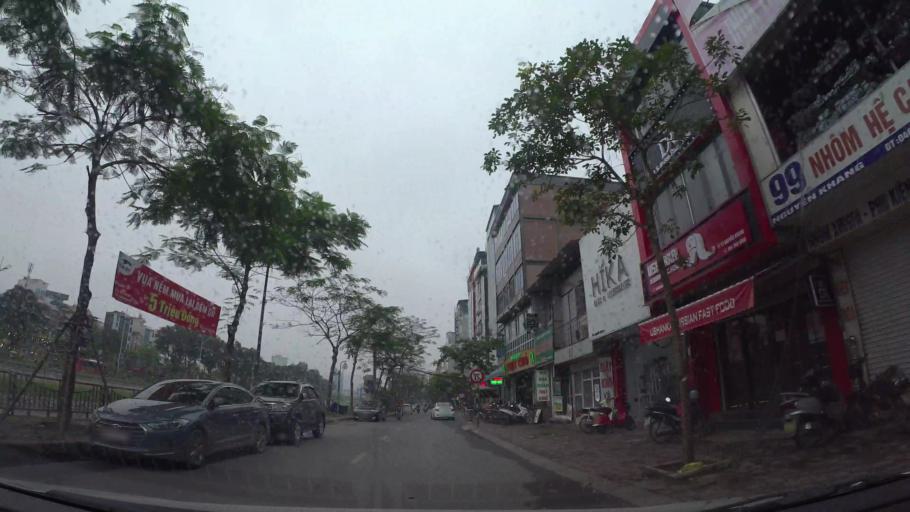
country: VN
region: Ha Noi
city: Cau Giay
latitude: 21.0193
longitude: 105.8015
